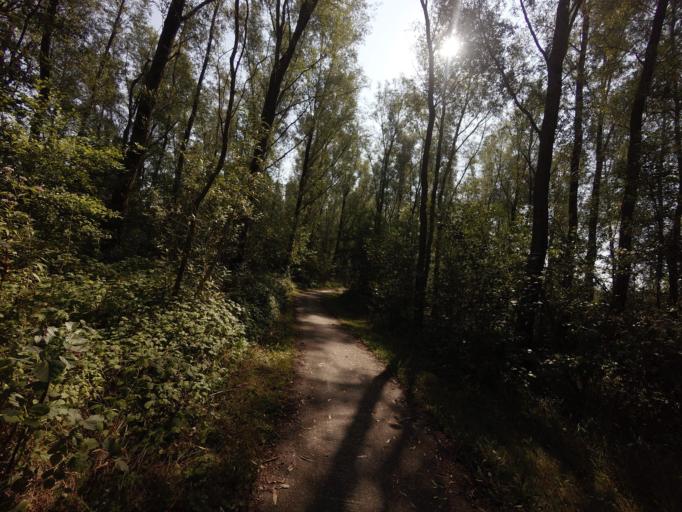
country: NL
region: Groningen
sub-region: Gemeente De Marne
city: Ulrum
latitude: 53.3916
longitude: 6.2574
